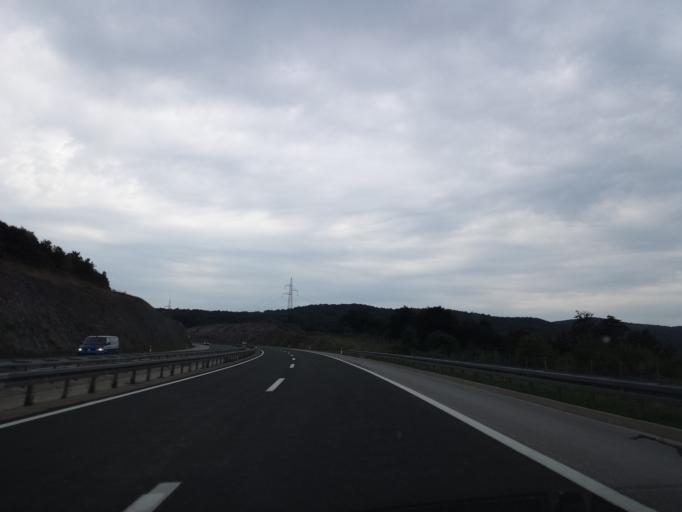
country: HR
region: Licko-Senjska
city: Brinje
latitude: 45.0529
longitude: 15.1886
